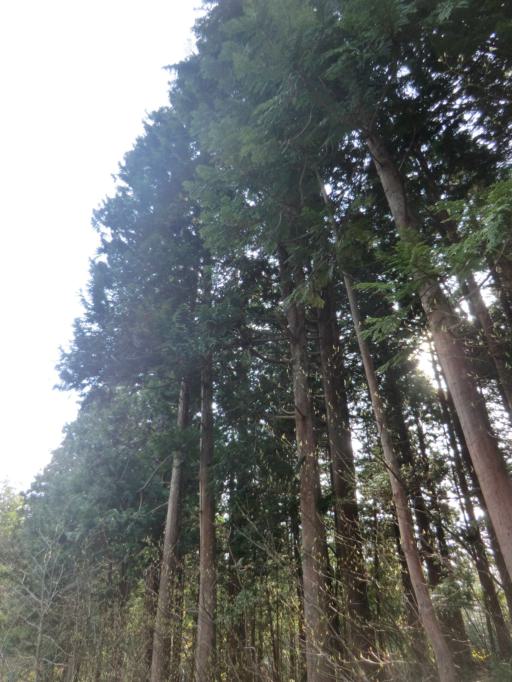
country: JP
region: Aomori
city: Mutsu
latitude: 41.3183
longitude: 141.1311
